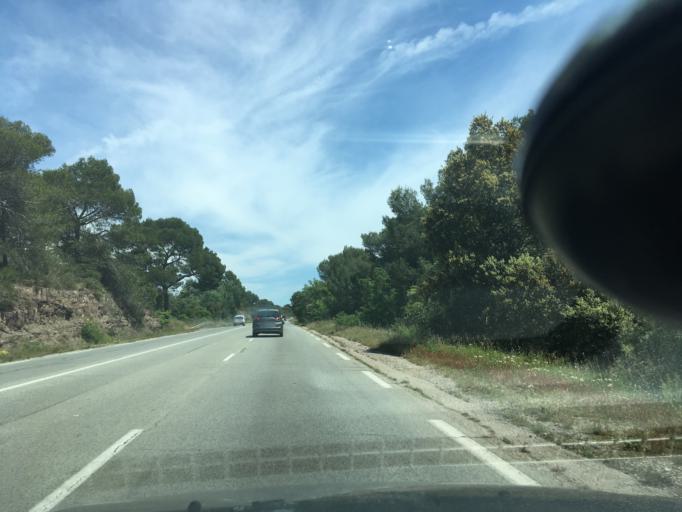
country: FR
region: Provence-Alpes-Cote d'Azur
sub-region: Departement du Var
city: Roquebrune-sur-Argens
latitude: 43.4664
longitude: 6.6150
